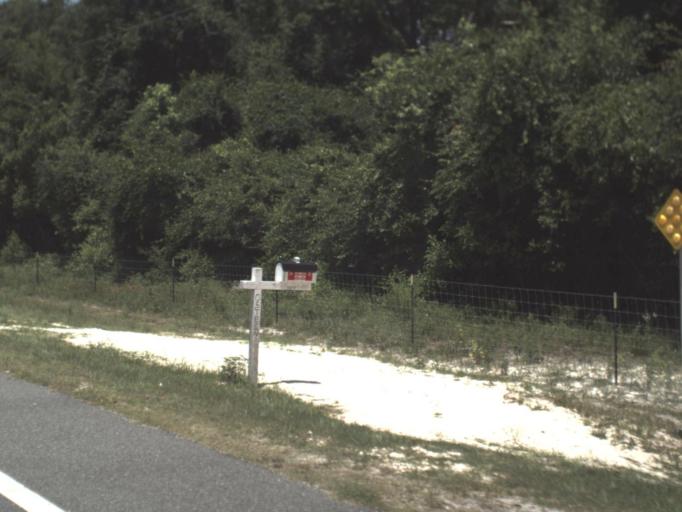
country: US
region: Florida
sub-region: Dixie County
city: Cross City
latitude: 29.6780
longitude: -82.9842
